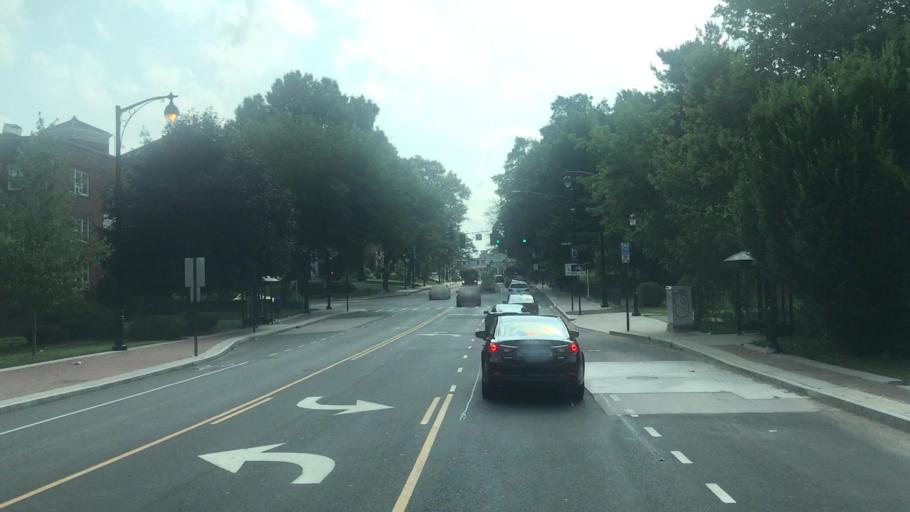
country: US
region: Connecticut
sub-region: Hartford County
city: Hartford
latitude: 41.7672
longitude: -72.7033
